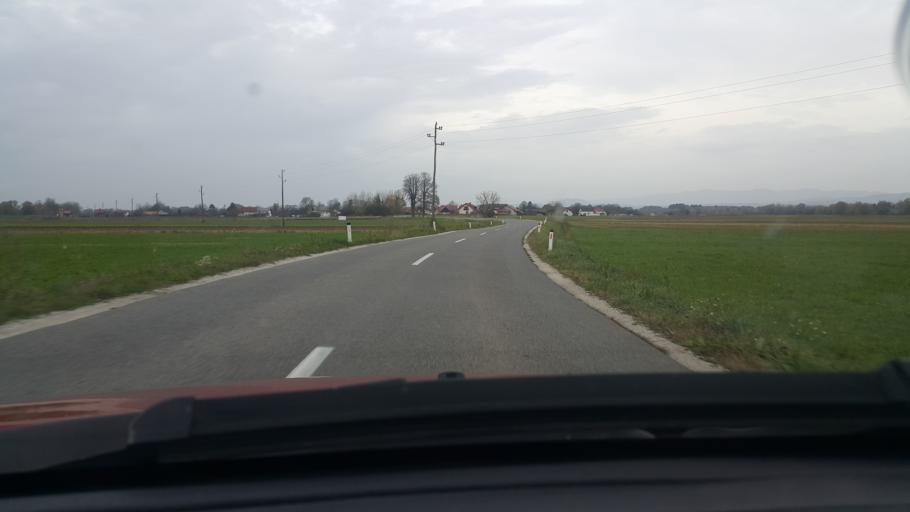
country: SI
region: Brezice
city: Brezice
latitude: 45.8962
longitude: 15.6393
